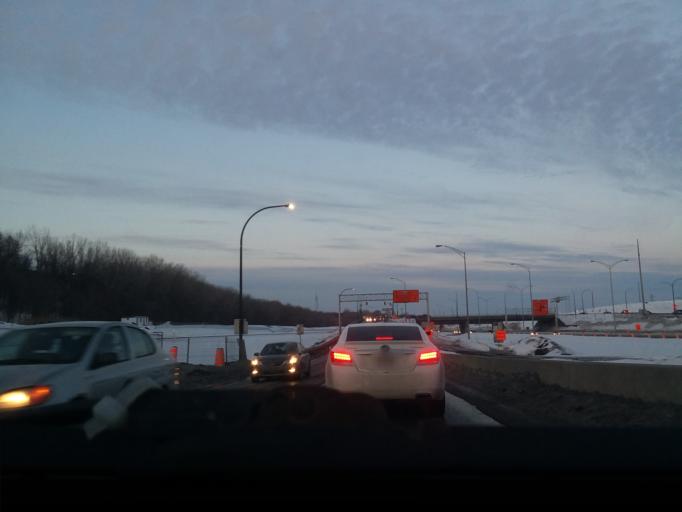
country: CA
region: Quebec
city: Montreal-Ouest
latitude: 45.4527
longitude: -73.6305
